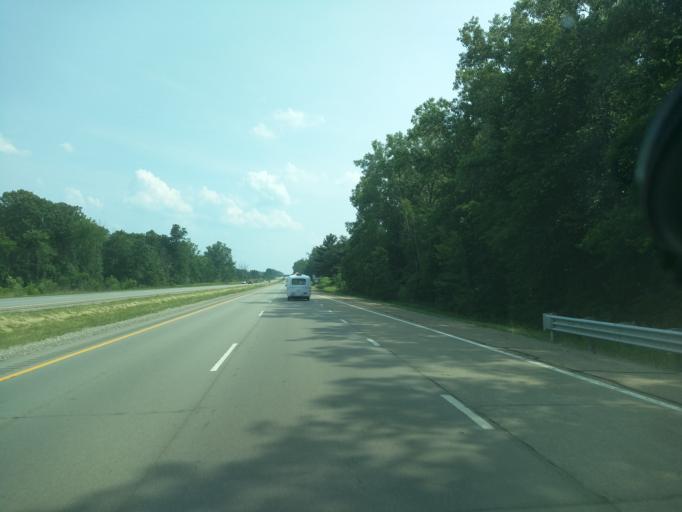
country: US
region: Michigan
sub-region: Ingham County
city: Leslie
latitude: 42.3589
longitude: -84.4291
